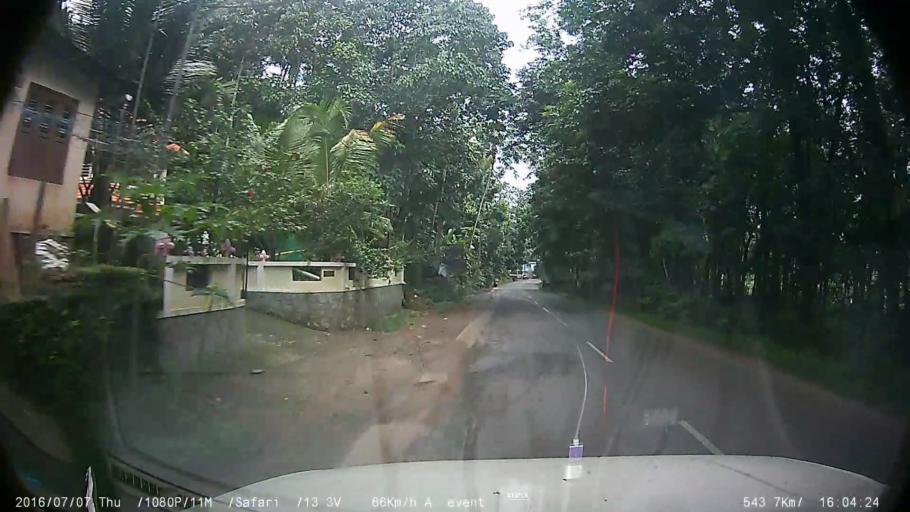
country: IN
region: Kerala
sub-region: Kottayam
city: Palackattumala
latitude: 9.8279
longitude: 76.6069
